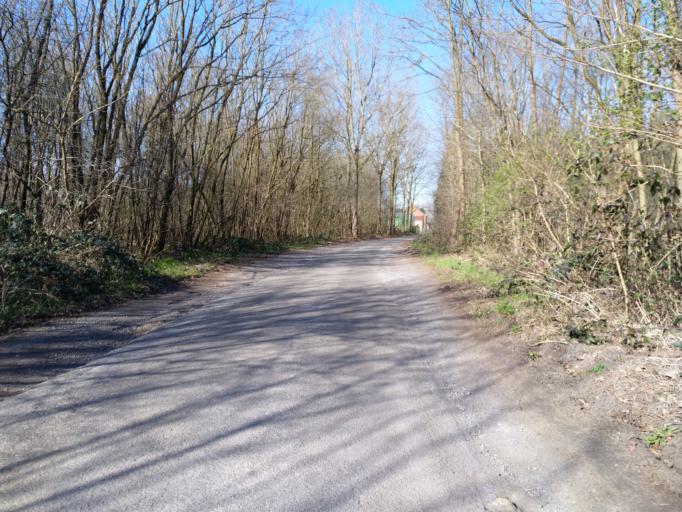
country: BE
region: Wallonia
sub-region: Province du Hainaut
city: Jurbise
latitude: 50.5061
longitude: 3.8794
